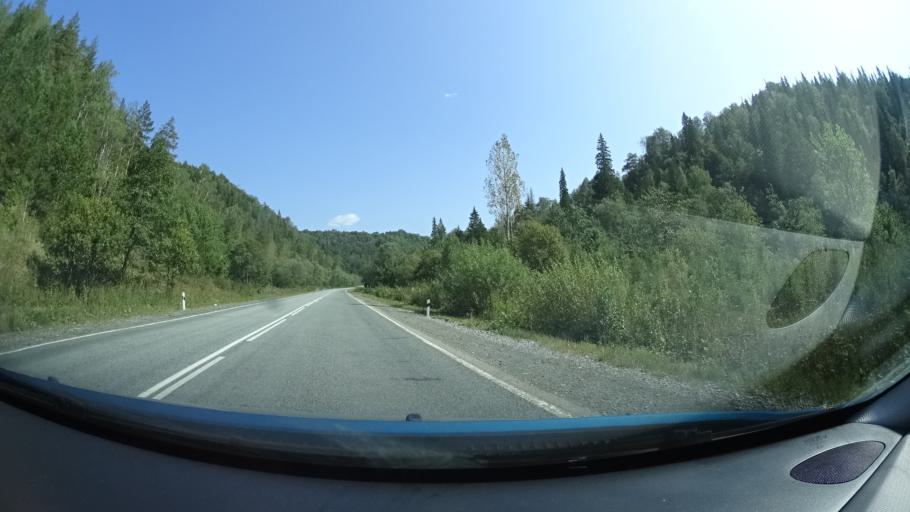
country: RU
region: Bashkortostan
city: Inzer
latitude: 54.3177
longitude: 57.1755
